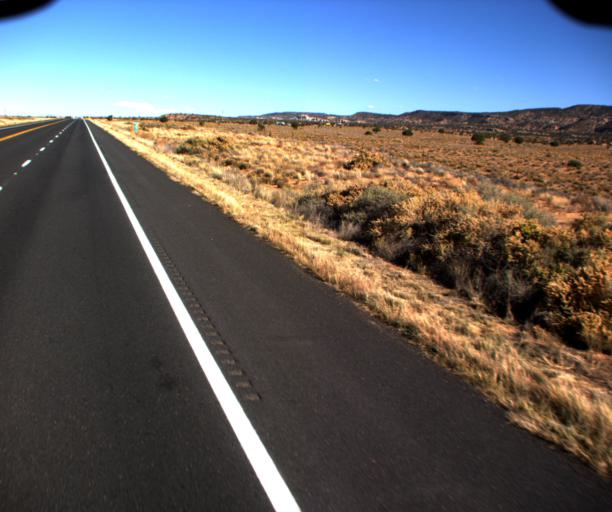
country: US
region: Arizona
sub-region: Coconino County
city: Kaibito
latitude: 36.3991
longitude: -110.8593
